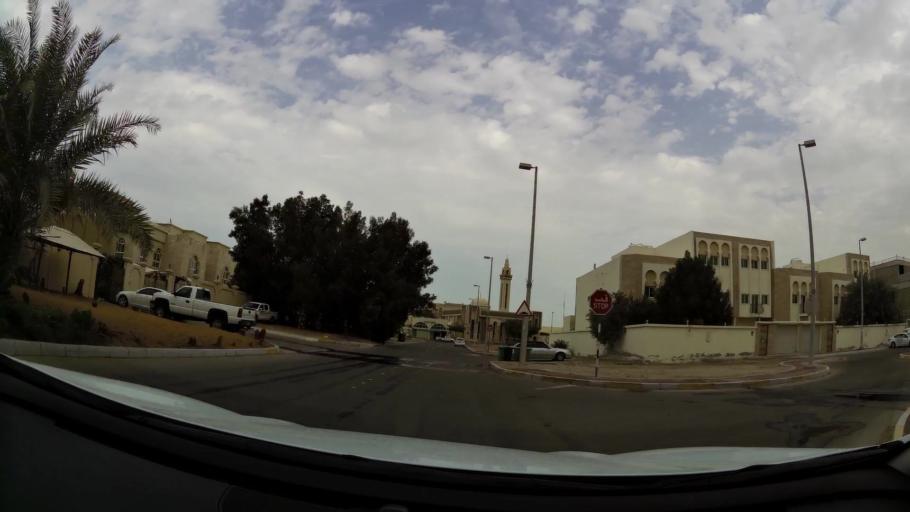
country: AE
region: Abu Dhabi
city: Abu Dhabi
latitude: 24.4341
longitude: 54.4418
